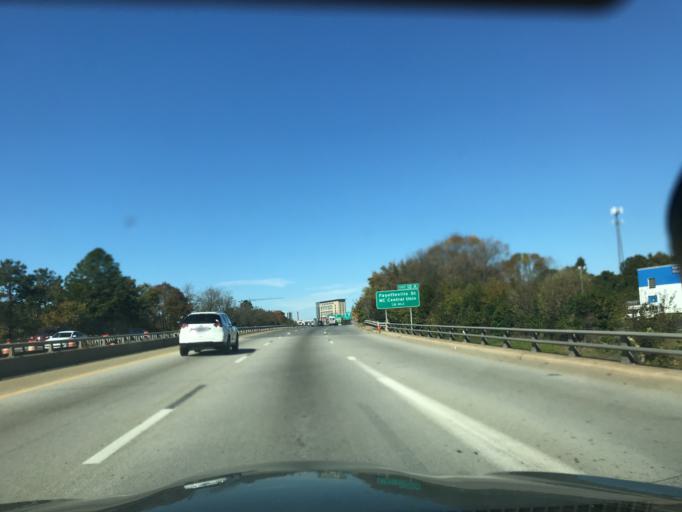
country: US
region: North Carolina
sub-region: Durham County
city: Durham
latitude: 35.9837
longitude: -78.8930
